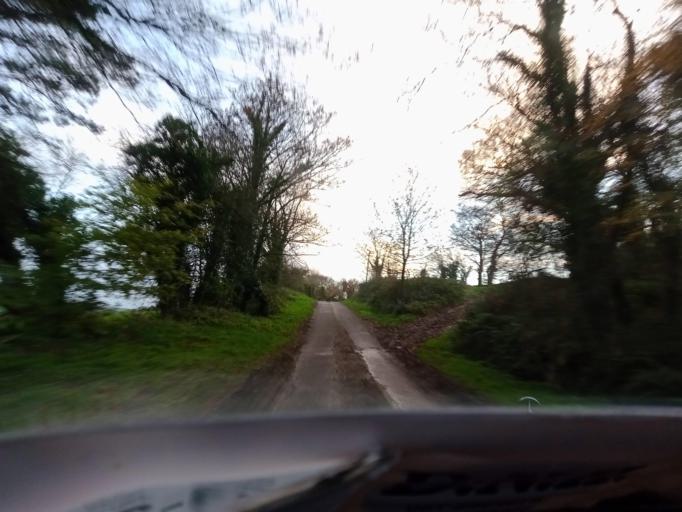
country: IE
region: Leinster
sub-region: Loch Garman
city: New Ross
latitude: 52.3381
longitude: -7.0131
